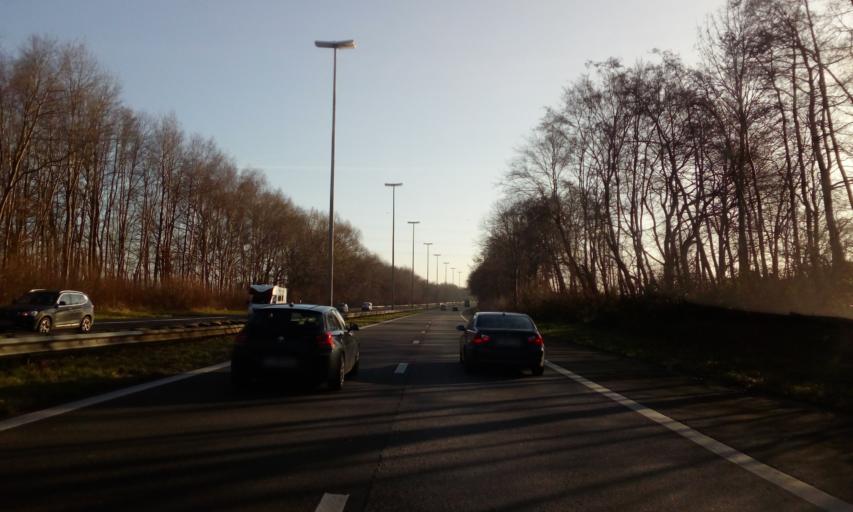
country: BE
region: Wallonia
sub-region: Province du Hainaut
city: Pont-a-Celles
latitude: 50.5541
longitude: 4.3637
